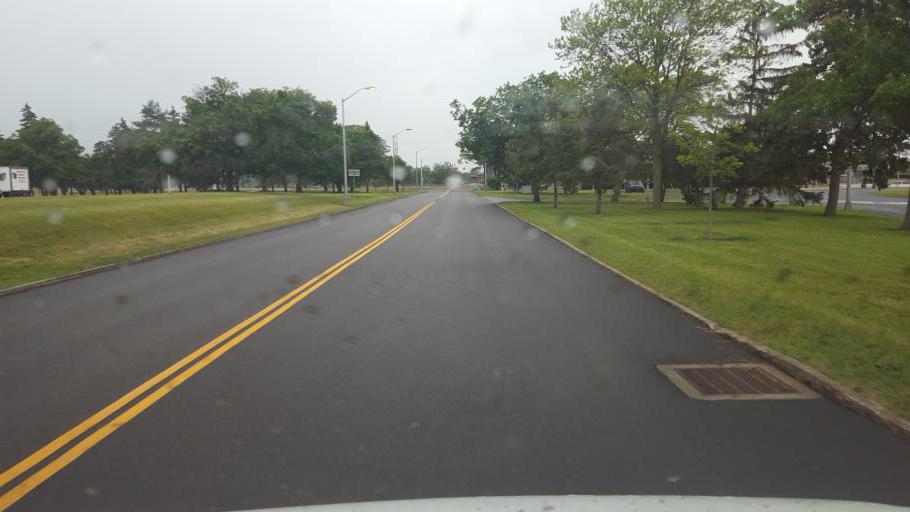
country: US
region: New York
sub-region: Niagara County
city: Lewiston
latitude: 43.1401
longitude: -79.0373
